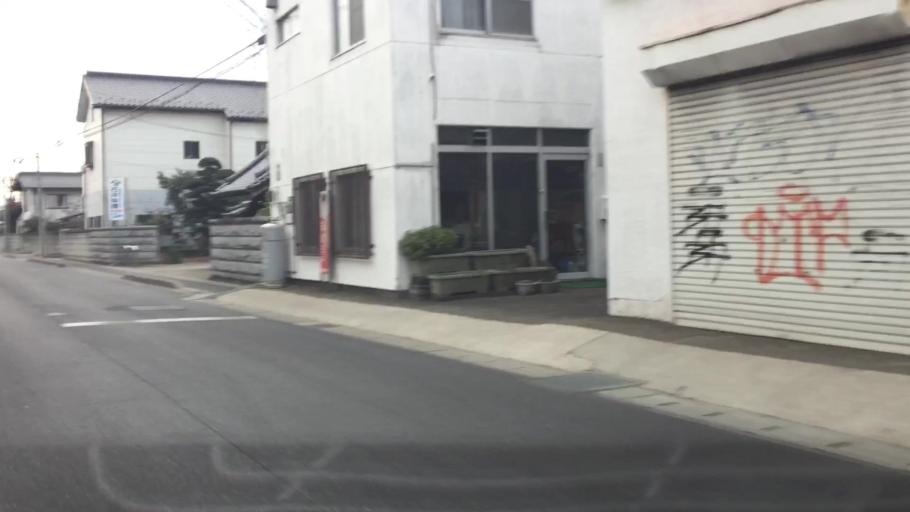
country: JP
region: Chiba
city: Shiroi
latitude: 35.7869
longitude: 140.0023
